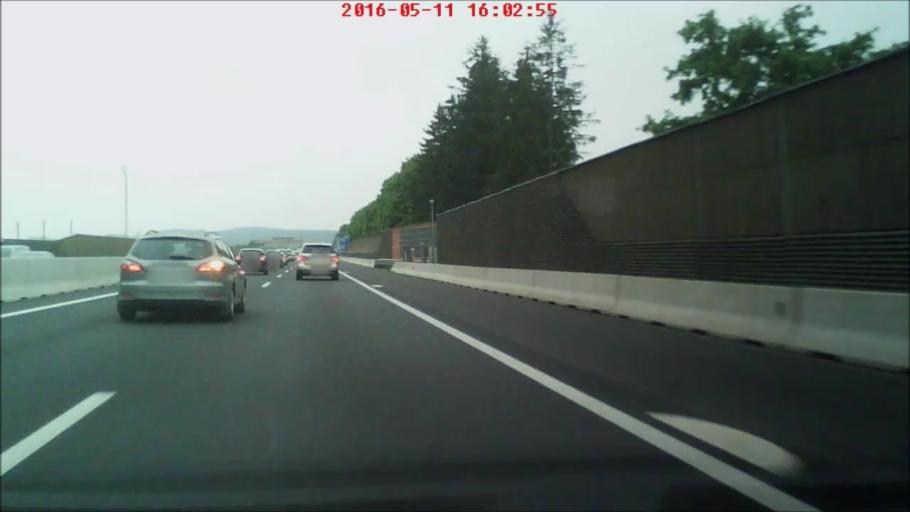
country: AT
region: Styria
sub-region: Politischer Bezirk Leibnitz
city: Weitendorf
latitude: 46.9071
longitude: 15.4721
